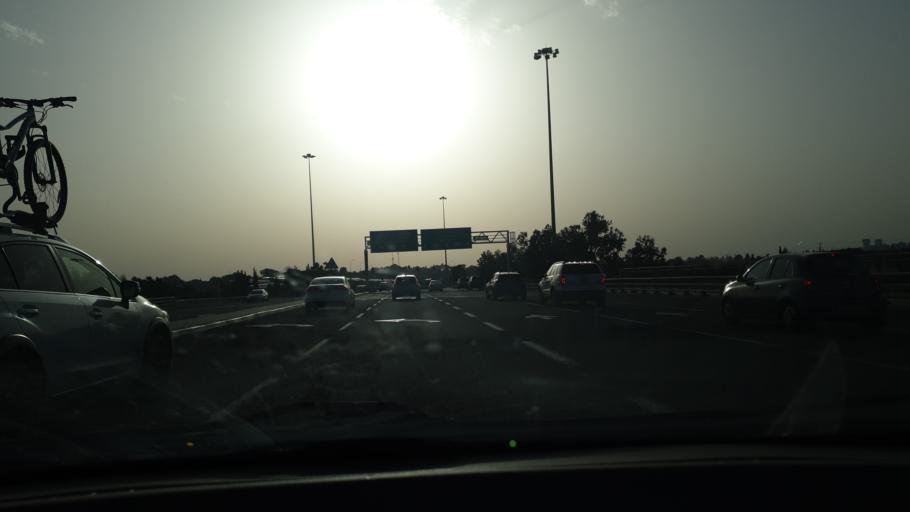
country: IL
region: Central District
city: Even Yehuda
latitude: 32.2554
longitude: 34.8912
